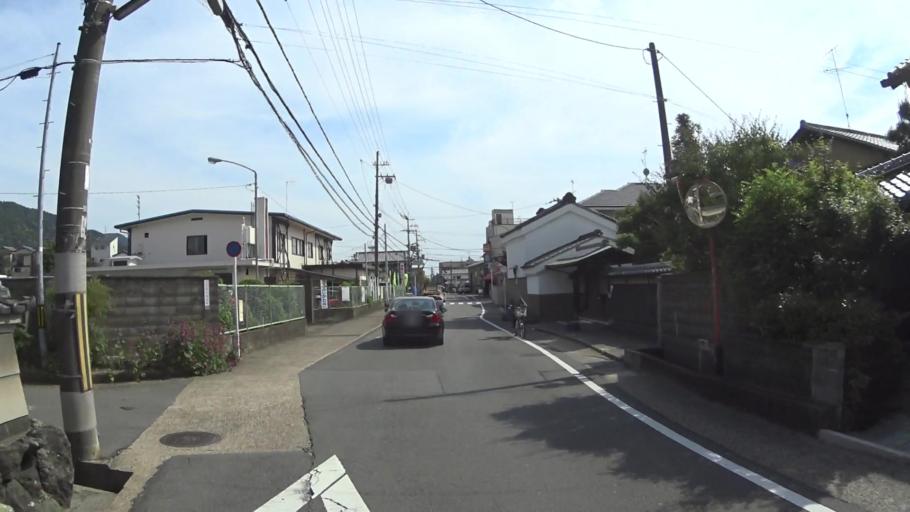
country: JP
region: Shiga Prefecture
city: Otsu-shi
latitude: 34.9714
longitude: 135.8213
